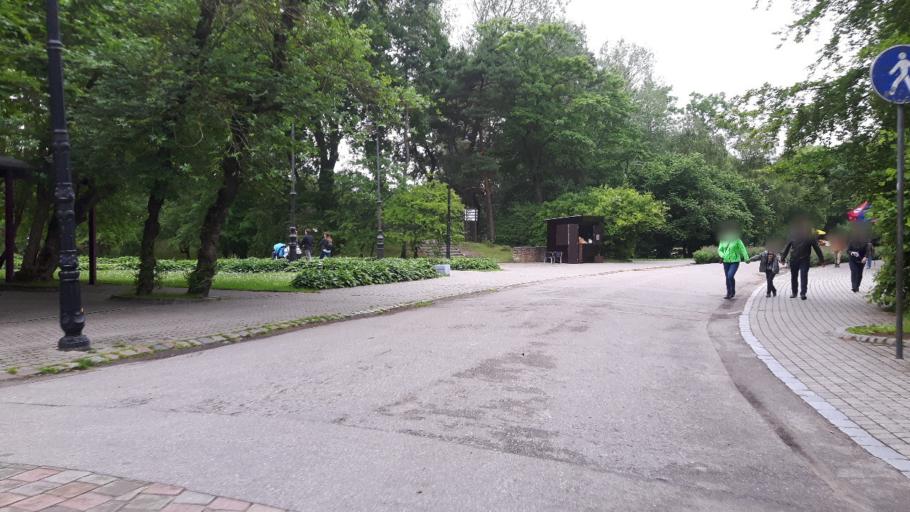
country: LV
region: Liepaja
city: Liepaja
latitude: 56.5046
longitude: 20.9963
